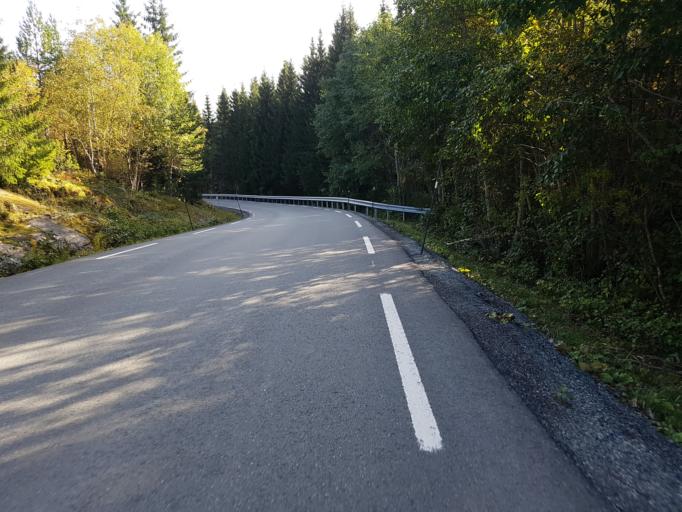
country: NO
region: Sor-Trondelag
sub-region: Malvik
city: Malvik
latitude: 63.3694
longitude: 10.6163
